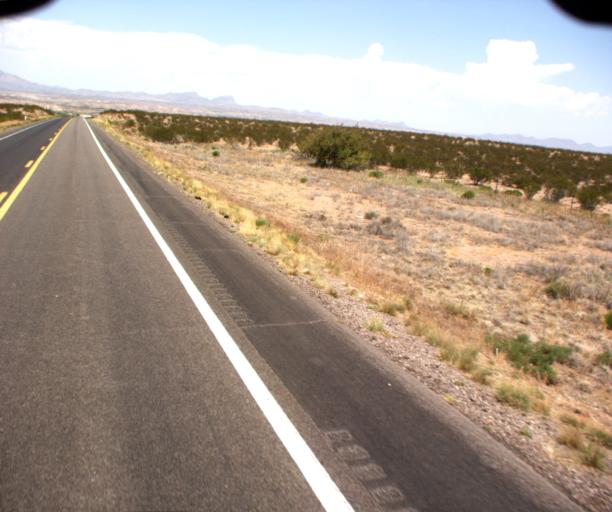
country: US
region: Arizona
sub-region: Greenlee County
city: Clifton
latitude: 32.7332
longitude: -109.1511
